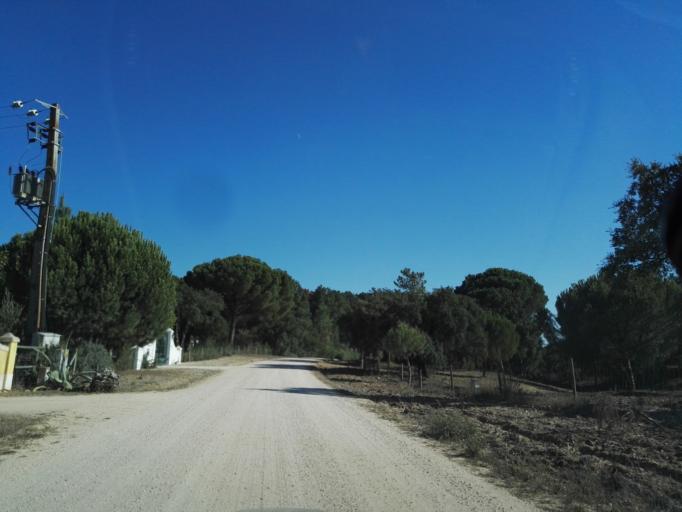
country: PT
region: Santarem
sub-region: Benavente
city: Poceirao
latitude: 38.8767
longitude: -8.7400
